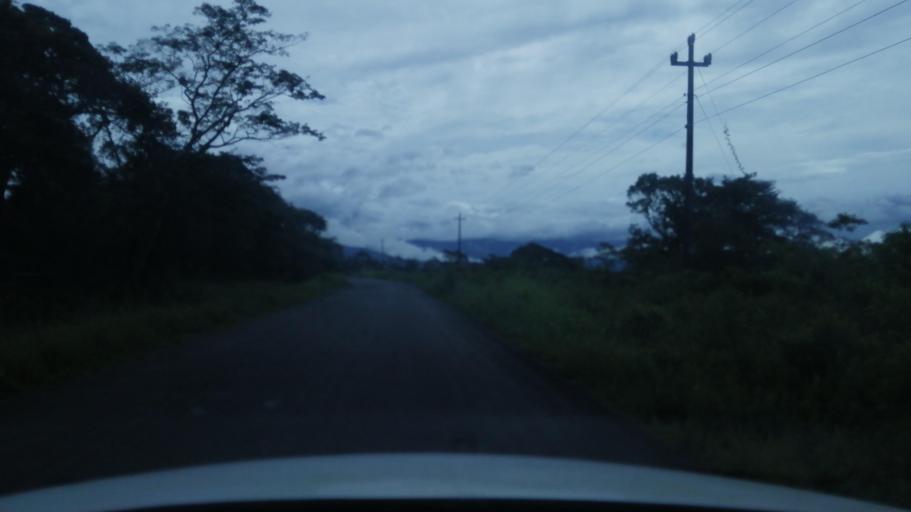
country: PA
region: Chiriqui
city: Potrerillos Abajo
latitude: 8.6708
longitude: -82.4394
